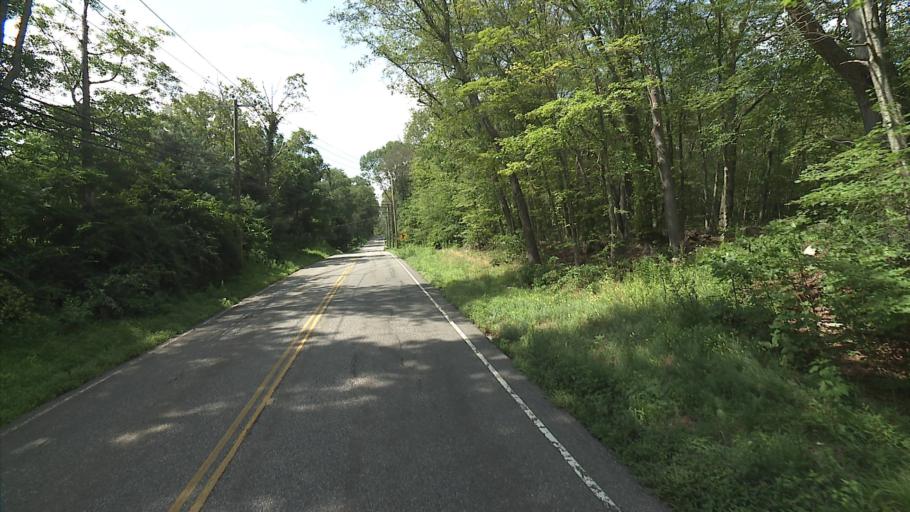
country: US
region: Connecticut
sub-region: New London County
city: Montville Center
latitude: 41.5023
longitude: -72.2346
